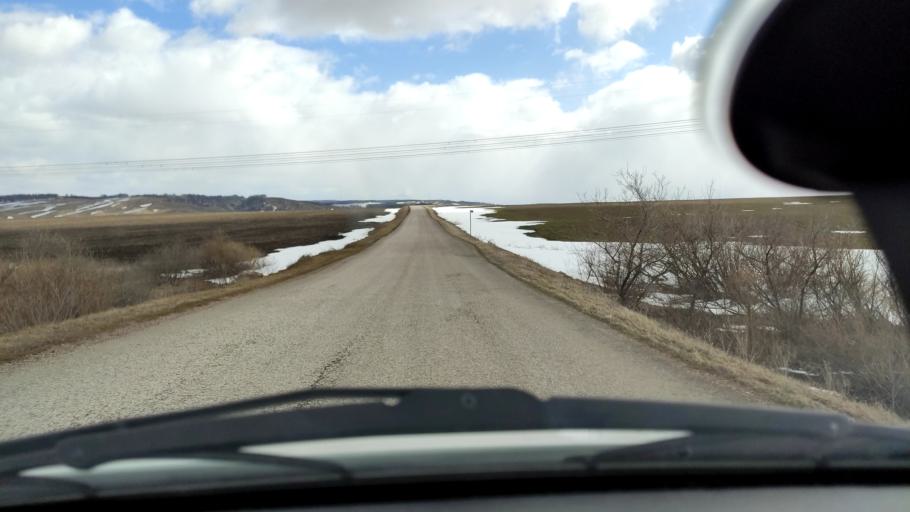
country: RU
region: Bashkortostan
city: Tolbazy
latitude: 54.1707
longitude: 55.9201
